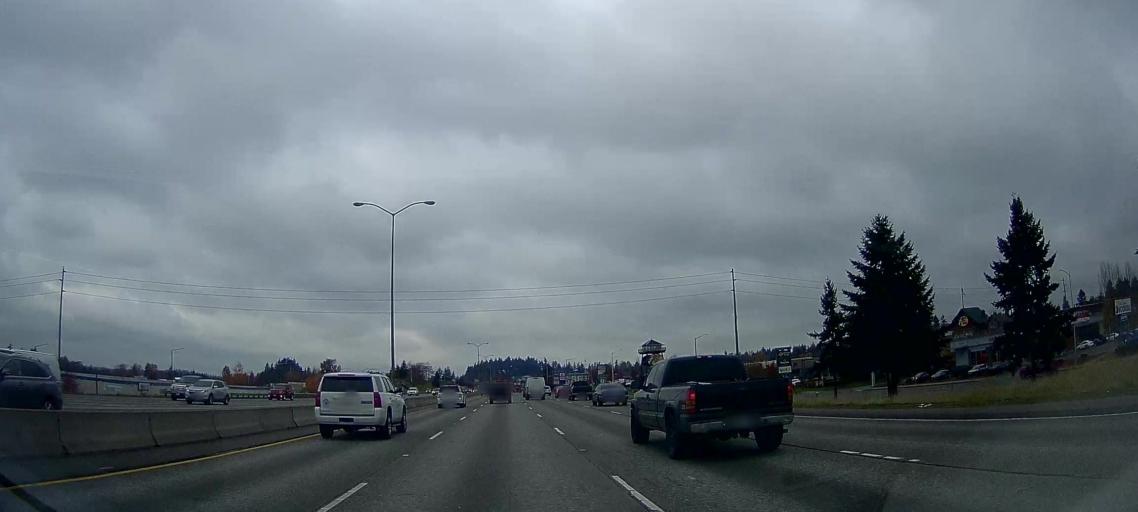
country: US
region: Washington
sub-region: Pierce County
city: Parkland
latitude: 47.1843
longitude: -122.4636
